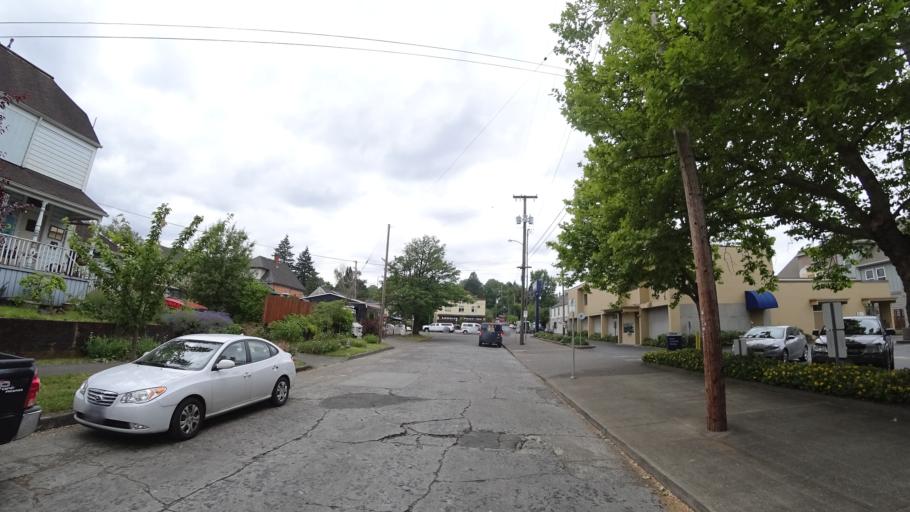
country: US
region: Oregon
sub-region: Multnomah County
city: Portland
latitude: 45.4996
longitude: -122.6534
